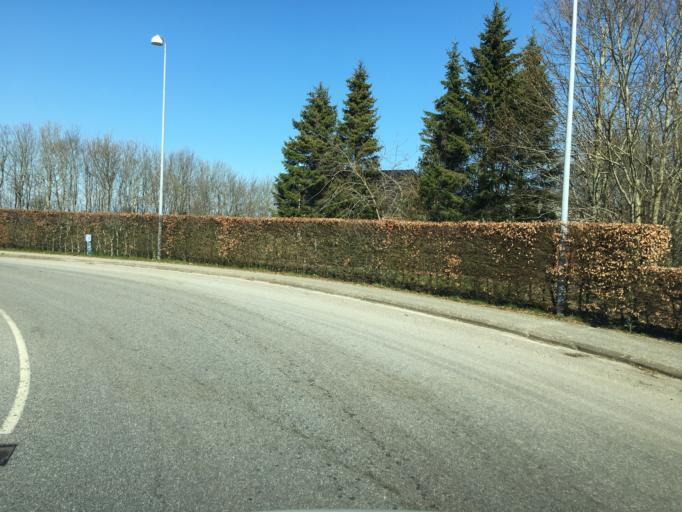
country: DK
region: South Denmark
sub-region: Aabenraa Kommune
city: Rodekro
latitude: 55.0211
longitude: 9.3202
